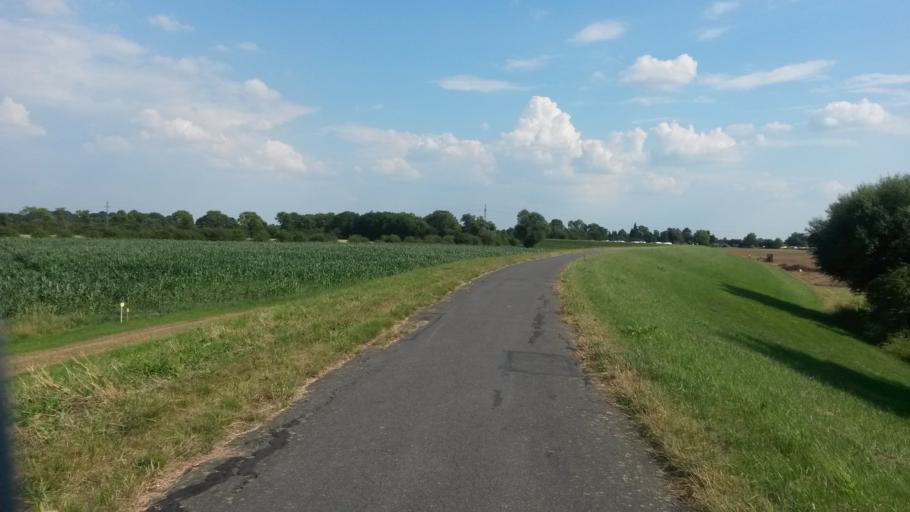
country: DE
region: Lower Saxony
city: Riede
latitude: 53.0160
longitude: 8.9218
